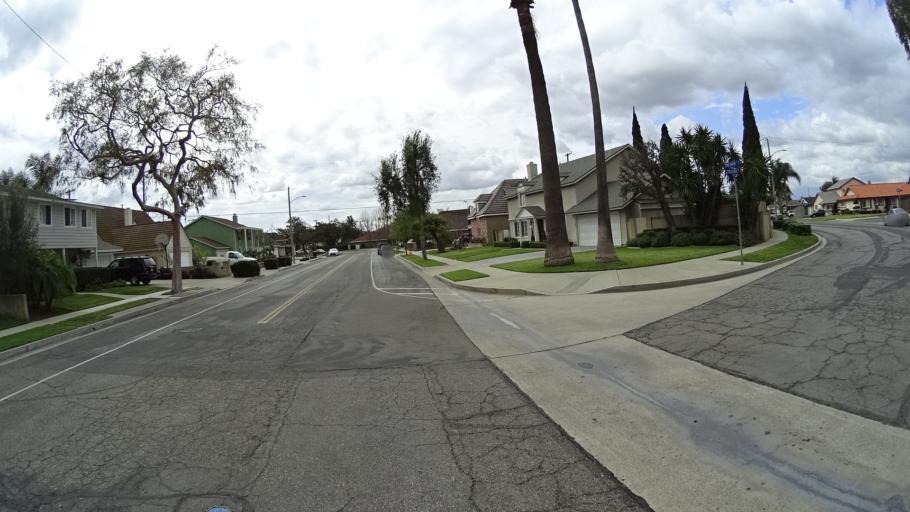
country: US
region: California
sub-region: Orange County
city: Placentia
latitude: 33.8406
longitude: -117.8642
